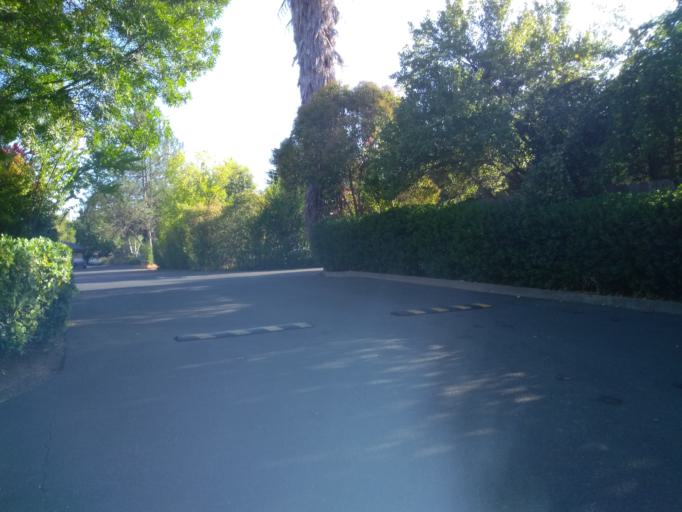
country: US
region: California
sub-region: Mendocino County
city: Ukiah
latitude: 39.1366
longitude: -123.2087
